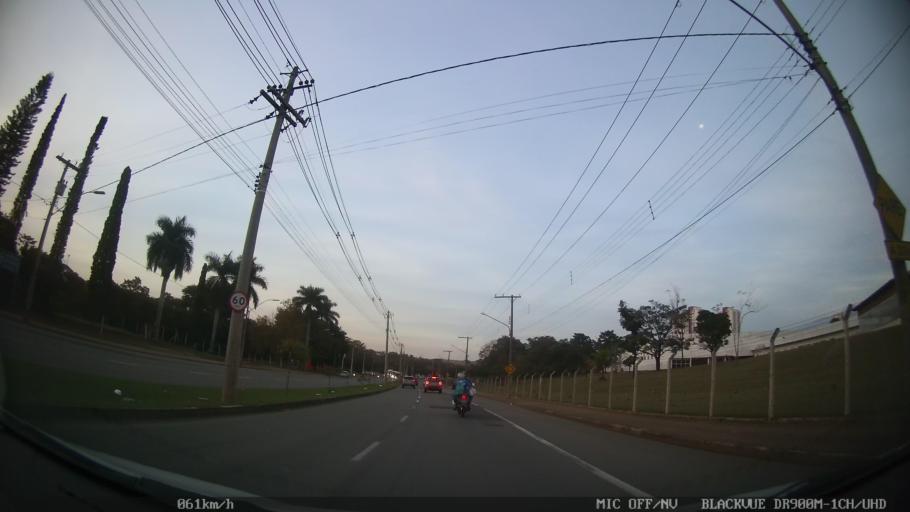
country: BR
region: Sao Paulo
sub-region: Limeira
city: Limeira
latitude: -22.5464
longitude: -47.4232
